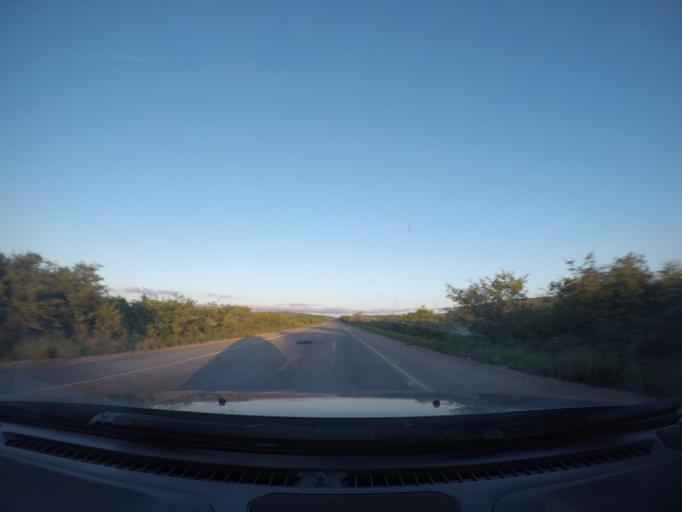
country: BR
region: Bahia
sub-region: Seabra
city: Seabra
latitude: -12.3913
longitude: -41.9088
